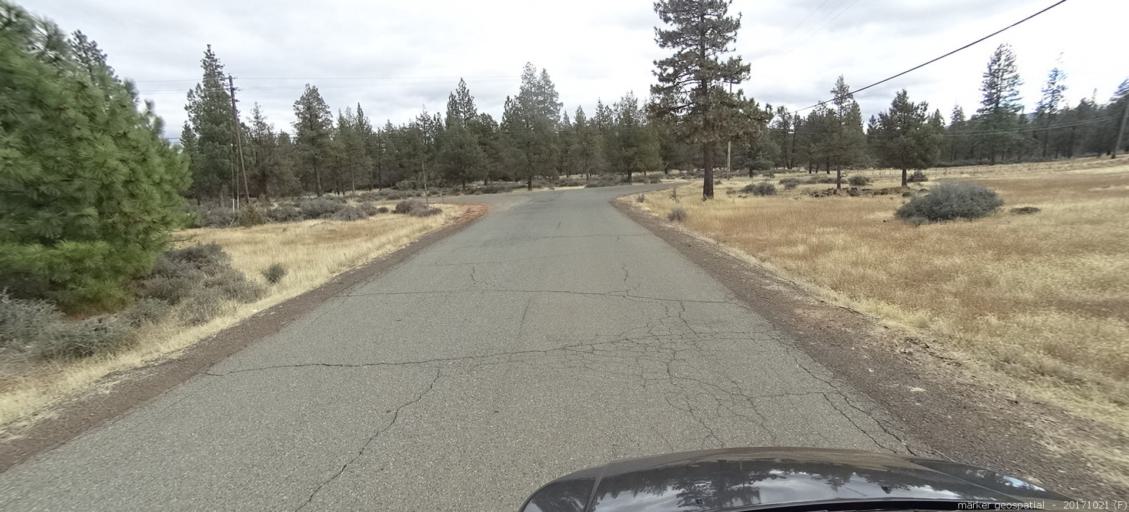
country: US
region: California
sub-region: Shasta County
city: Burney
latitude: 40.9255
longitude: -121.6465
